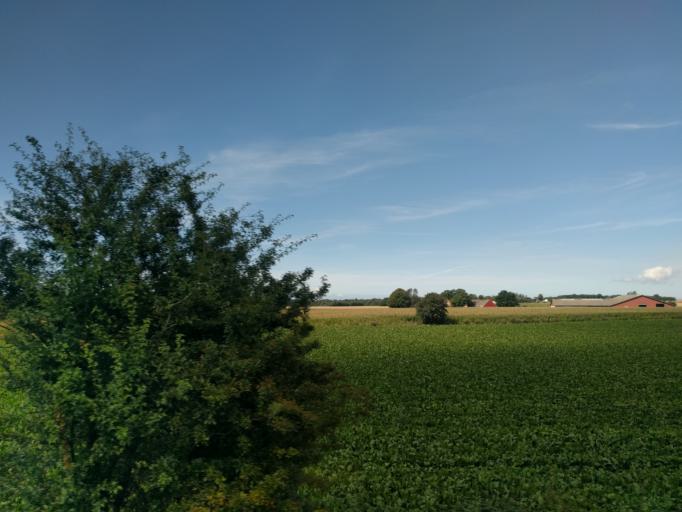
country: DK
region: Zealand
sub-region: Slagelse Kommune
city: Forlev
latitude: 55.3698
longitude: 11.2455
